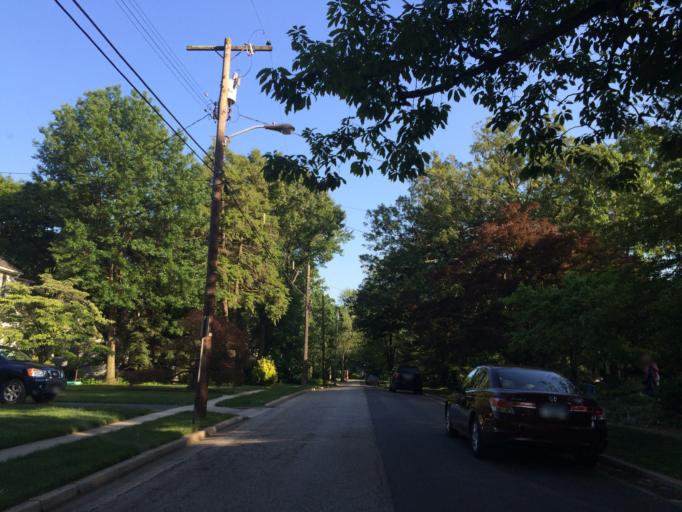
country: US
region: Maryland
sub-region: Baltimore County
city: Catonsville
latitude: 39.2664
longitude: -76.7392
